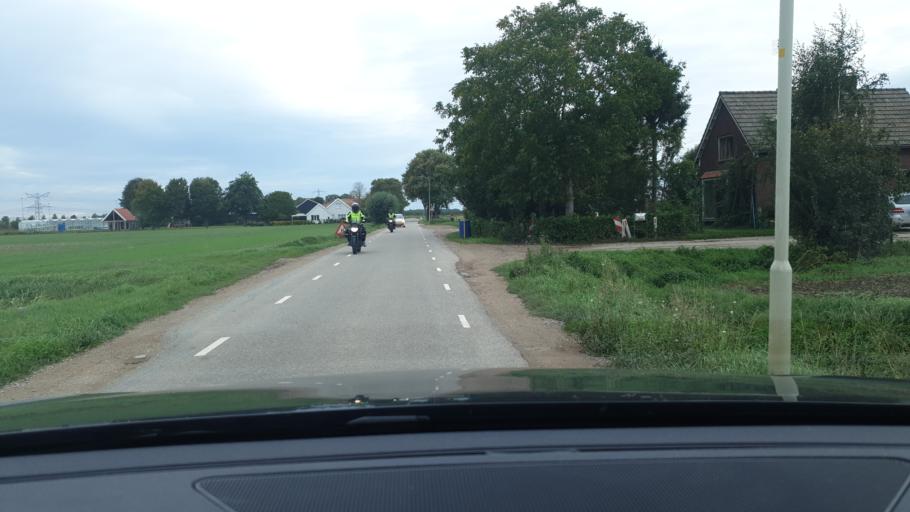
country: NL
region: Gelderland
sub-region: Gemeente Overbetuwe
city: Oosterhout
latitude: 51.8981
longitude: 5.8236
